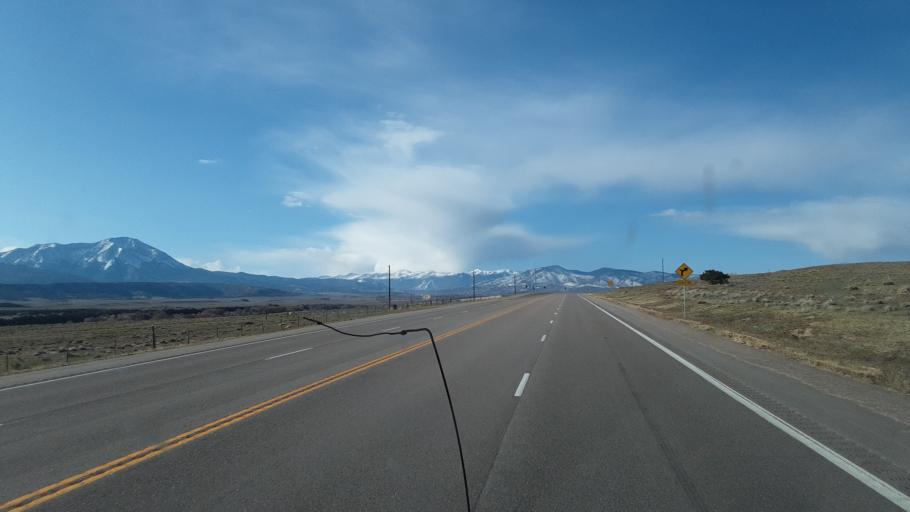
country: US
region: Colorado
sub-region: Huerfano County
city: Walsenburg
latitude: 37.5623
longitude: -104.9337
